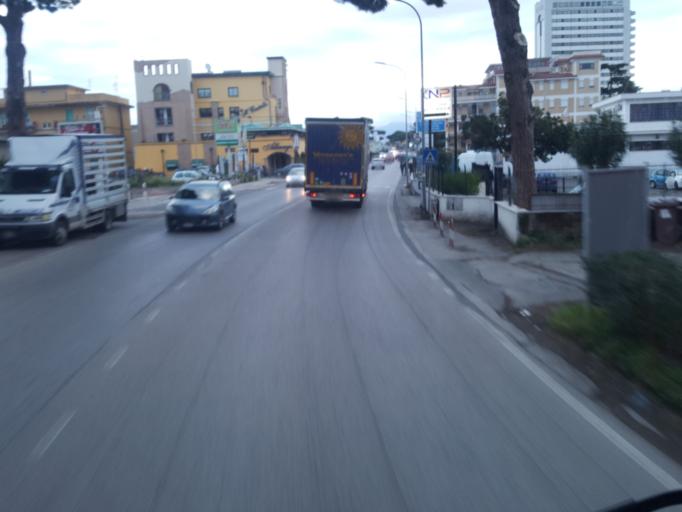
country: IT
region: Latium
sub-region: Citta metropolitana di Roma Capitale
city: Area Produttiva
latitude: 41.6802
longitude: 12.5028
